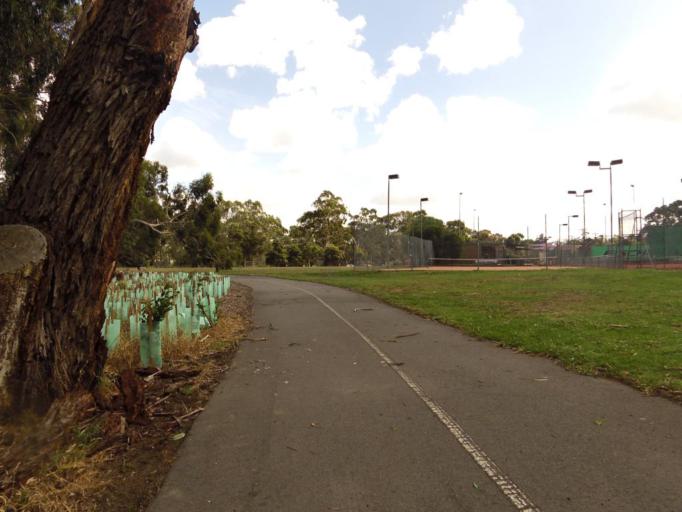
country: AU
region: Victoria
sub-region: Nillumbik
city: Eltham North
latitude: -37.7137
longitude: 145.1463
